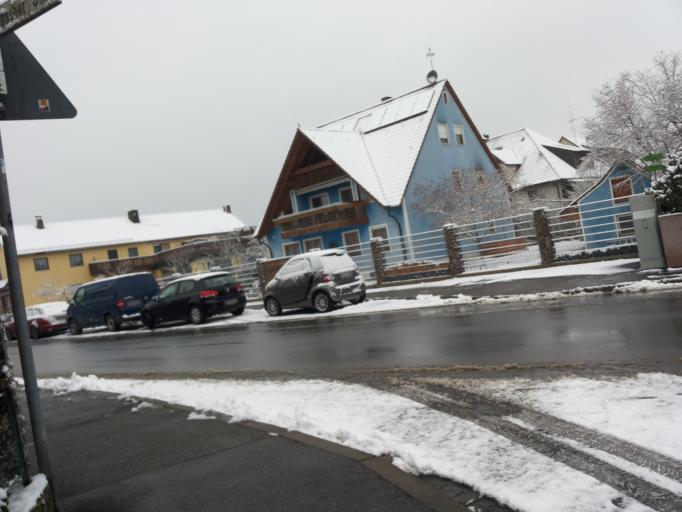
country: DE
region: Bavaria
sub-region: Regierungsbezirk Mittelfranken
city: Zirndorf
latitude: 49.4269
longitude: 10.9160
